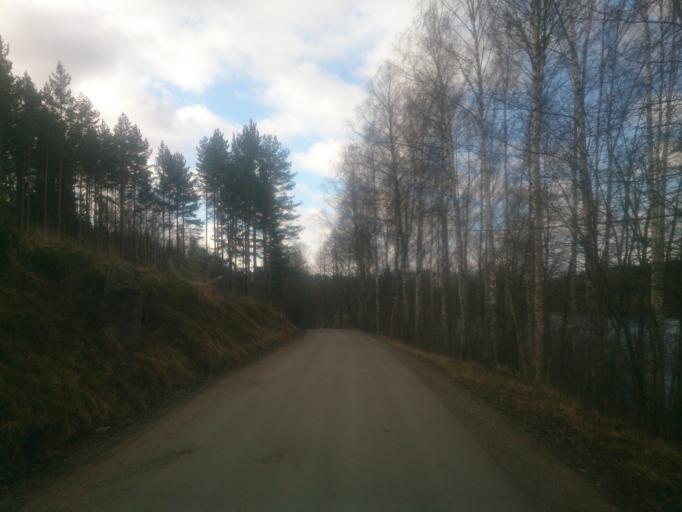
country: SE
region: OEstergoetland
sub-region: Atvidabergs Kommun
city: Atvidaberg
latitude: 58.1970
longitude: 16.1531
